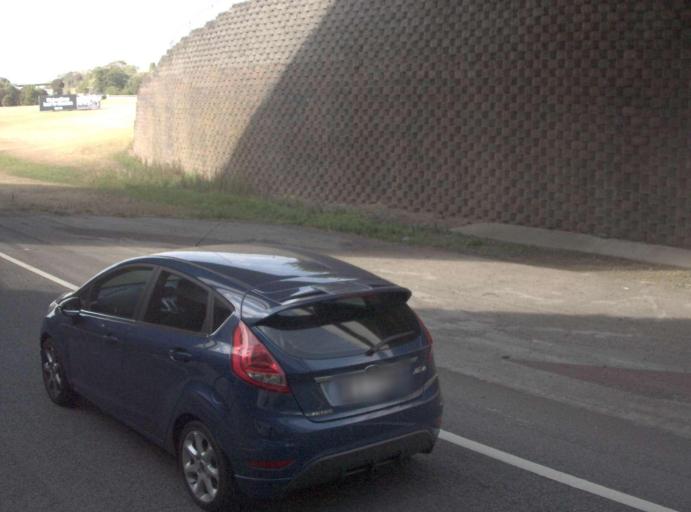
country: AU
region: Victoria
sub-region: Casey
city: Eumemmerring
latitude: -37.9910
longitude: 145.2547
